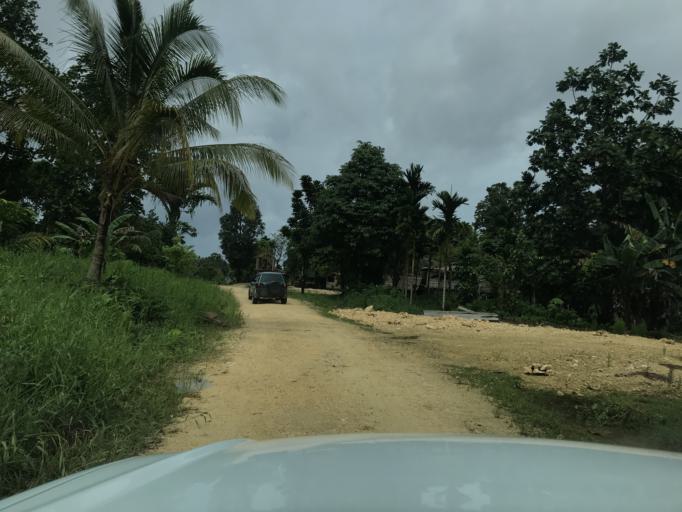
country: SB
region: Malaita
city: Auki
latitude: -8.6309
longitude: 160.6629
